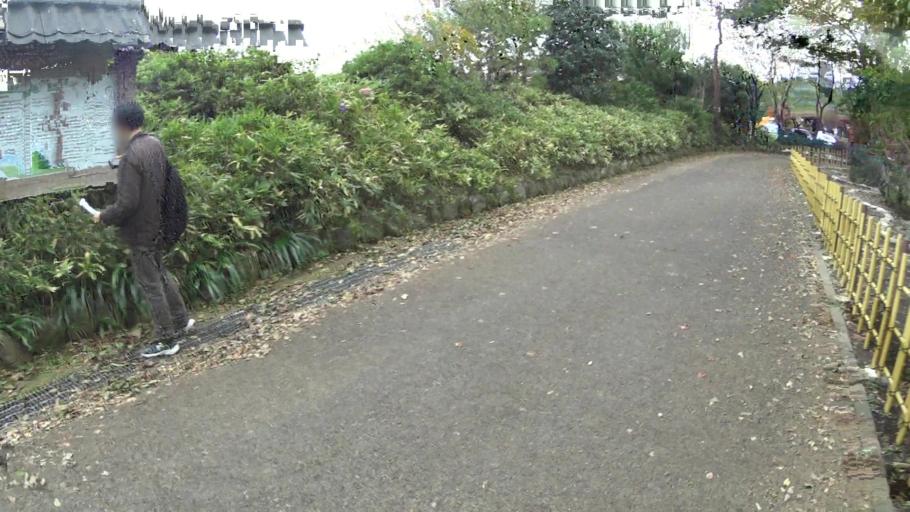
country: JP
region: Kanagawa
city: Hadano
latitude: 35.3942
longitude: 139.2239
